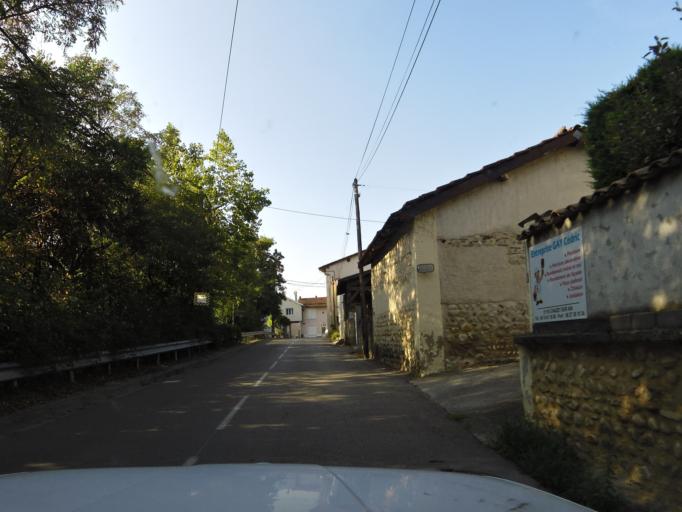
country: FR
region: Rhone-Alpes
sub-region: Departement de l'Ain
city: Chazey-sur-Ain
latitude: 45.8914
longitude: 5.2531
